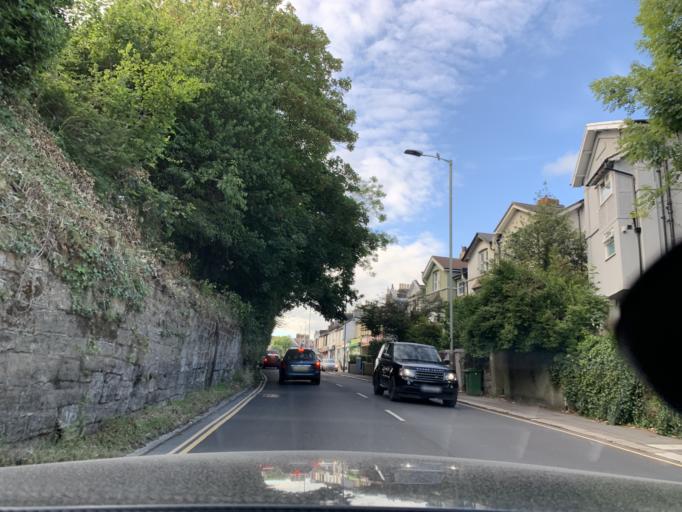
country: GB
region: England
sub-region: East Sussex
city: Saint Leonards-on-Sea
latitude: 50.8661
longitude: 0.5562
